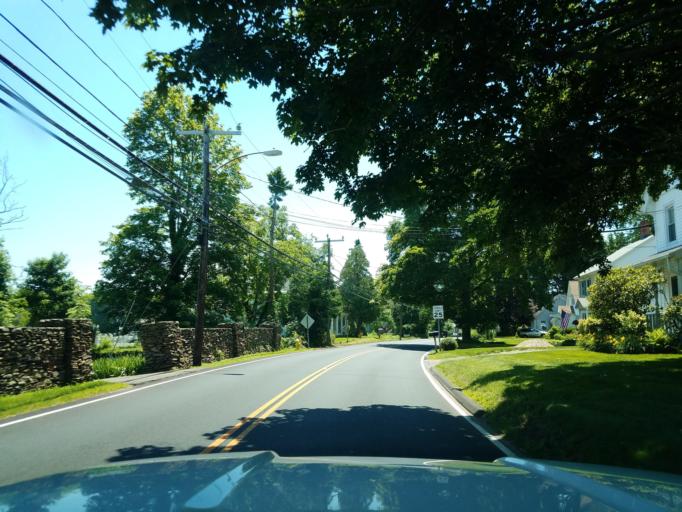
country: US
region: Connecticut
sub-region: New Haven County
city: Branford Center
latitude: 41.2731
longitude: -72.8045
